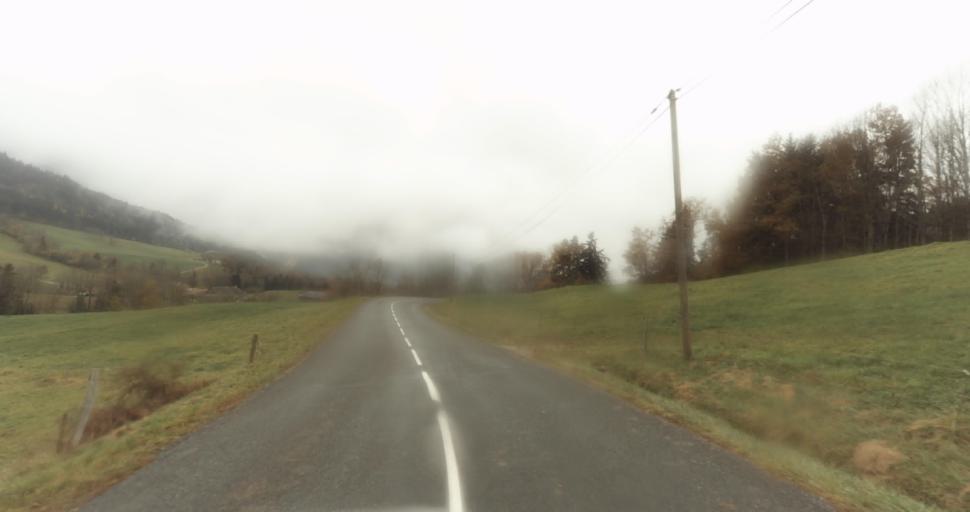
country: FR
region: Rhone-Alpes
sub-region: Departement de la Haute-Savoie
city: Thorens-Glieres
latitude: 46.0099
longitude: 6.2630
